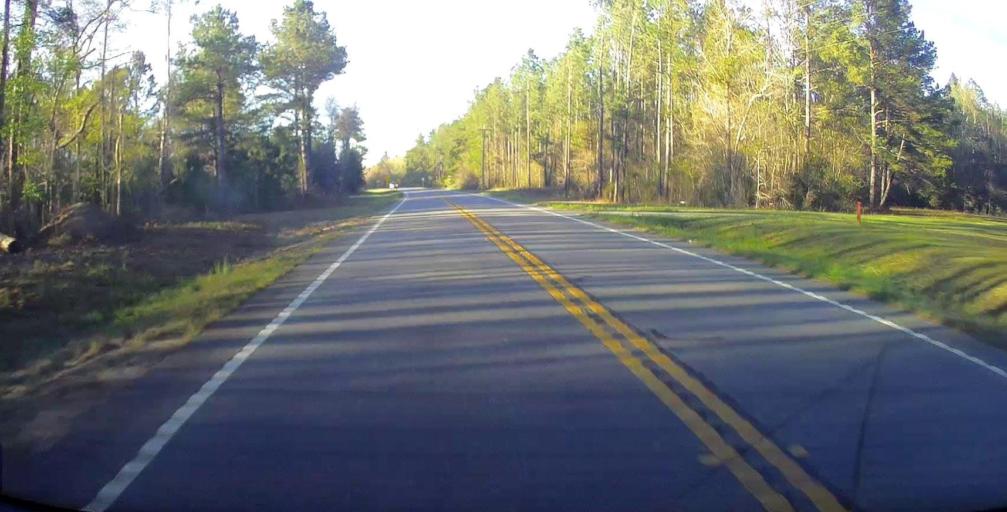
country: US
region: Georgia
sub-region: Wilcox County
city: Abbeville
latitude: 32.0106
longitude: -83.2482
